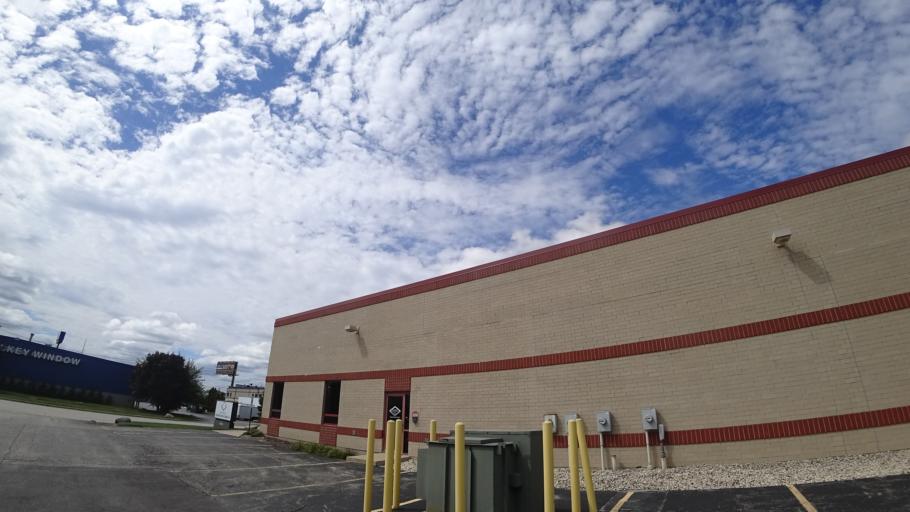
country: US
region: Illinois
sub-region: Cook County
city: Chicago Ridge
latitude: 41.7069
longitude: -87.7905
